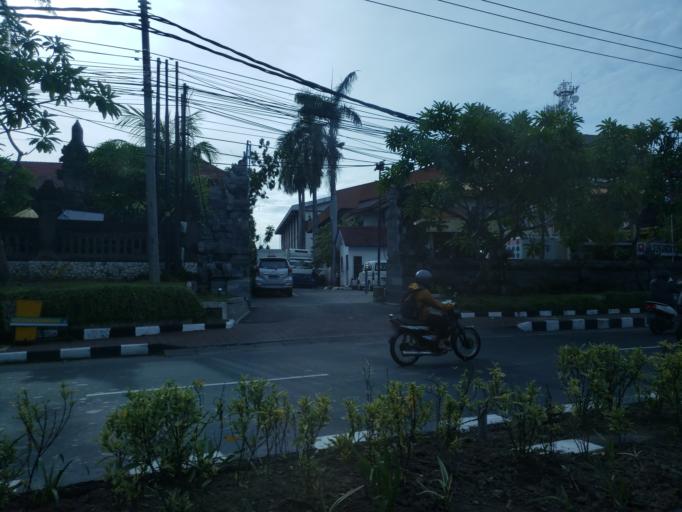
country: ID
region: Bali
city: Jabajero
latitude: -8.7363
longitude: 115.1796
